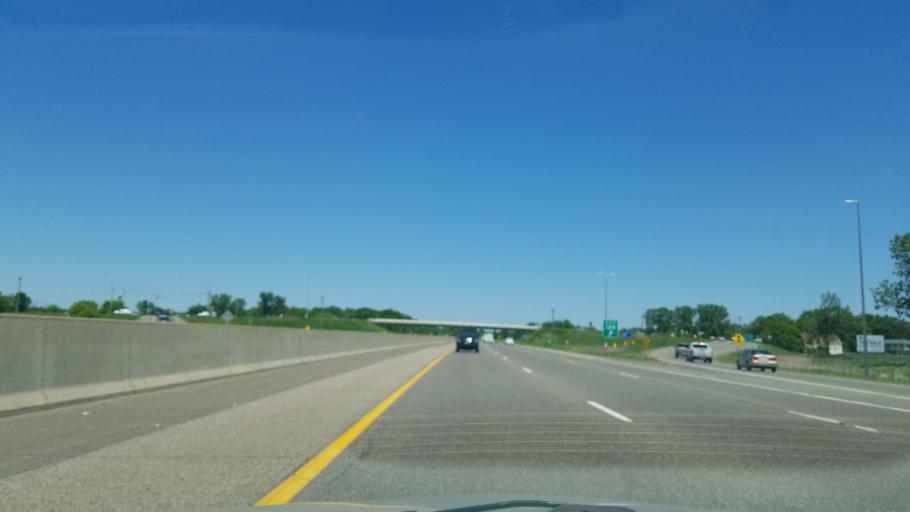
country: US
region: Minnesota
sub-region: Anoka County
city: Columbus
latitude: 45.2479
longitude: -93.0258
